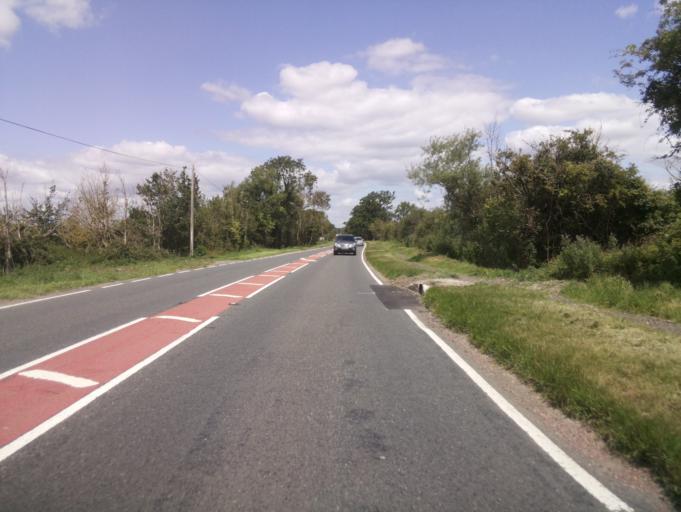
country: GB
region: England
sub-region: Buckinghamshire
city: Aylesbury
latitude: 51.8422
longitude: -0.8203
